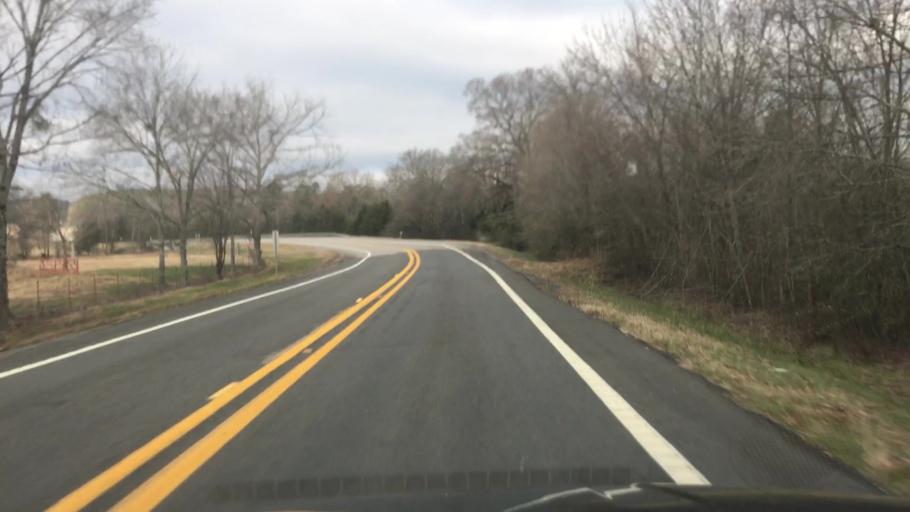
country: US
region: Arkansas
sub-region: Montgomery County
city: Mount Ida
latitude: 34.6581
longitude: -93.7615
